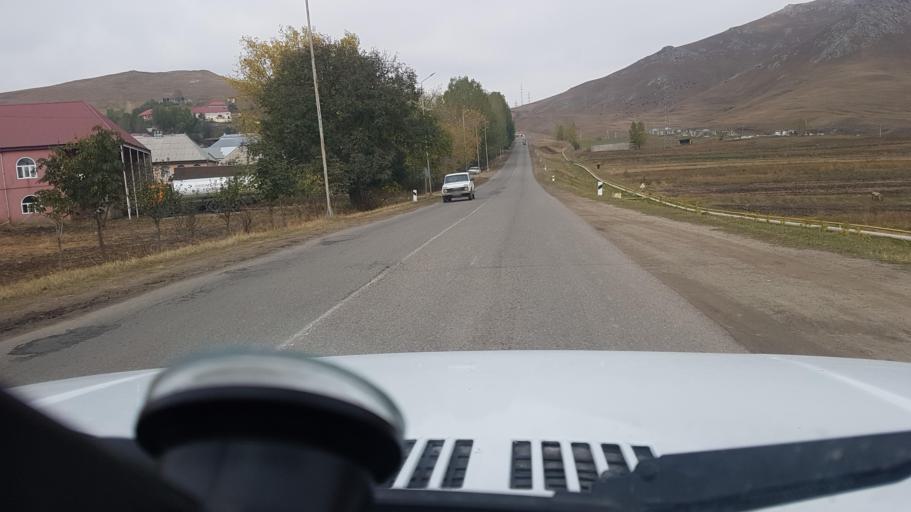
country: AZ
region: Gadabay Rayon
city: Ariqdam
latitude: 40.6070
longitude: 45.8124
